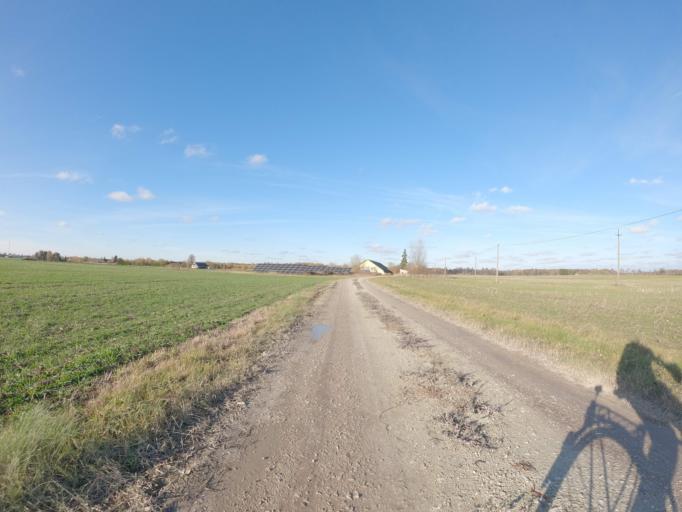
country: EE
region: Raplamaa
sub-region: Rapla vald
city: Rapla
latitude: 59.0257
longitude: 24.7945
